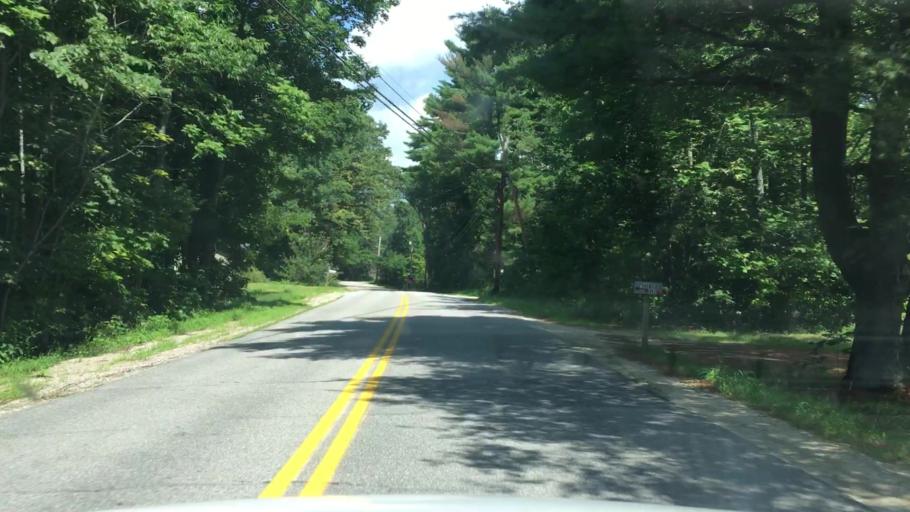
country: US
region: Maine
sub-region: Cumberland County
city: Raymond
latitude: 43.9465
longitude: -70.5255
